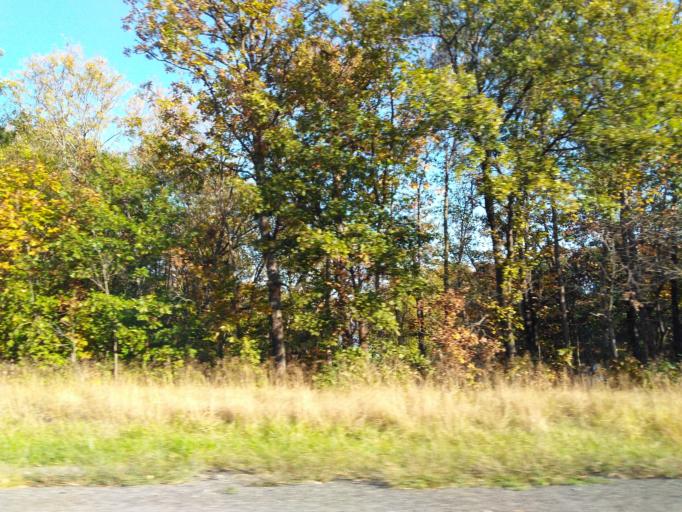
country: US
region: Illinois
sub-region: Madison County
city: Highland
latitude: 38.7865
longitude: -89.6998
